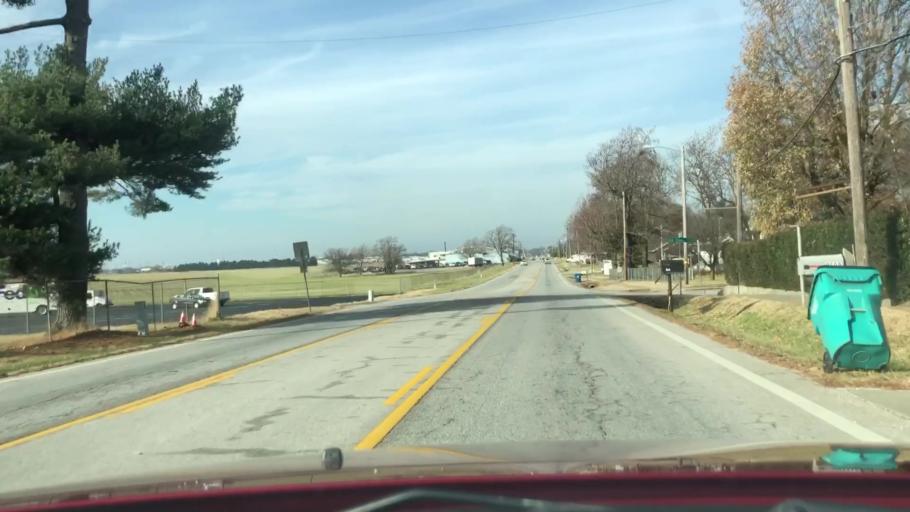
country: US
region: Missouri
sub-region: Greene County
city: Springfield
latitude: 37.2249
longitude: -93.2434
